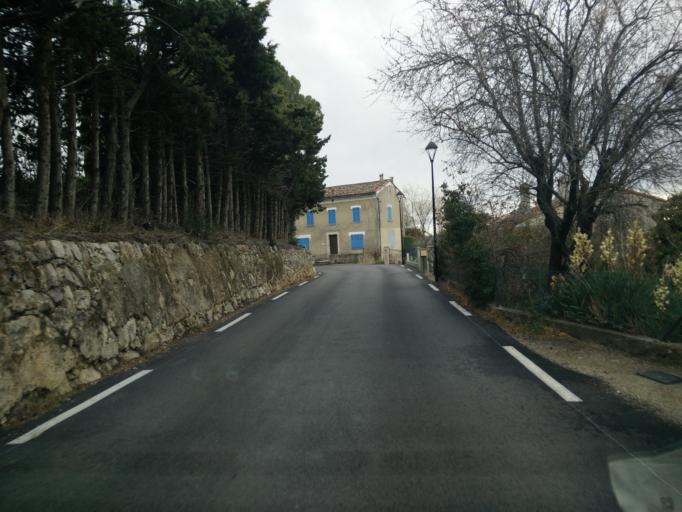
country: FR
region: Provence-Alpes-Cote d'Azur
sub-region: Departement du Var
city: Cotignac
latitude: 43.5256
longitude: 6.1531
